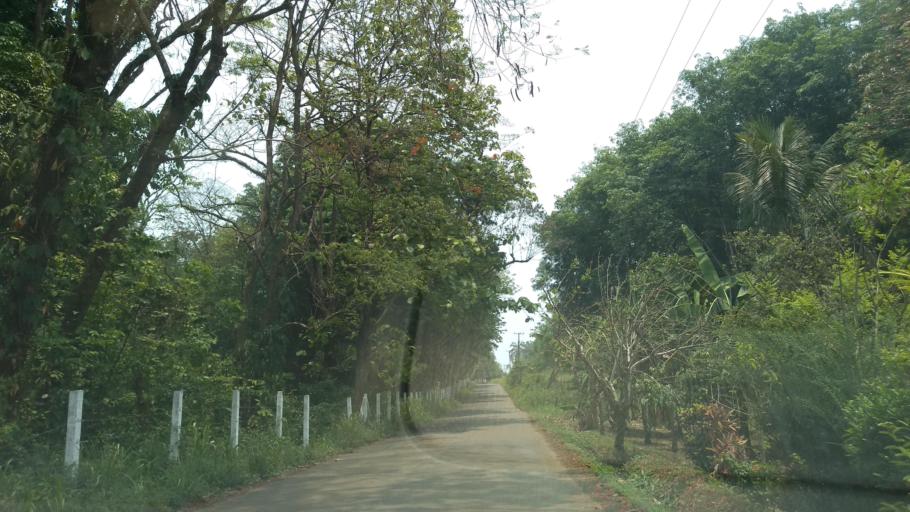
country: MX
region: Veracruz
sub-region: Tezonapa
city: Laguna Chica (Pueblo Nuevo)
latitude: 18.5133
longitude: -96.7604
